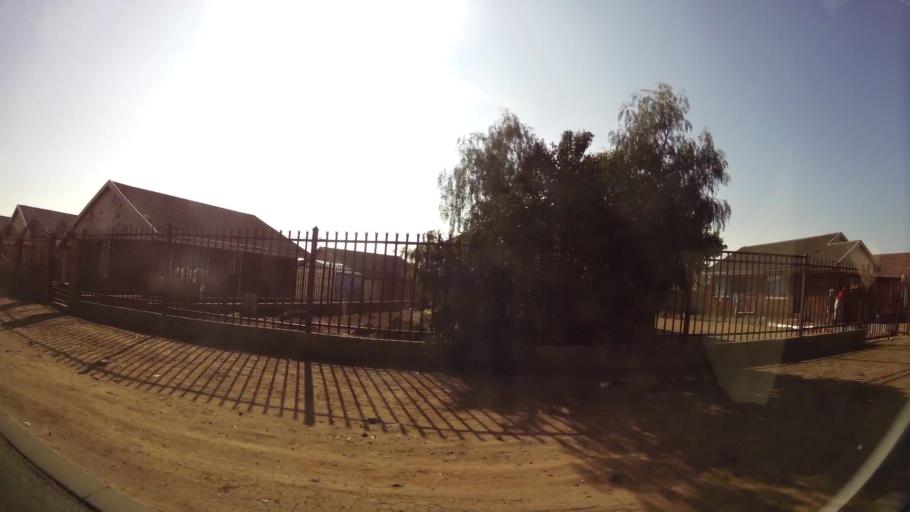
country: ZA
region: Orange Free State
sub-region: Mangaung Metropolitan Municipality
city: Bloemfontein
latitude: -29.1921
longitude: 26.2241
